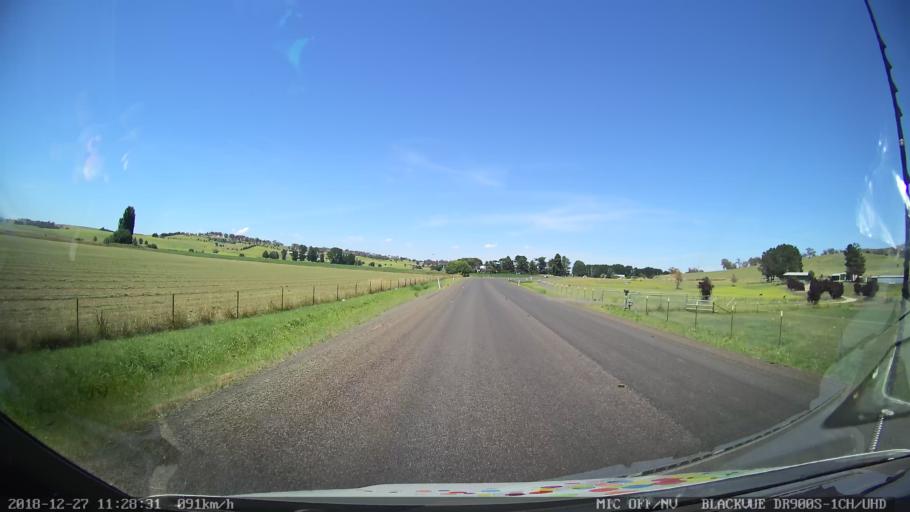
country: AU
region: New South Wales
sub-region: Bathurst Regional
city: Perthville
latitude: -33.4774
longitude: 149.5630
